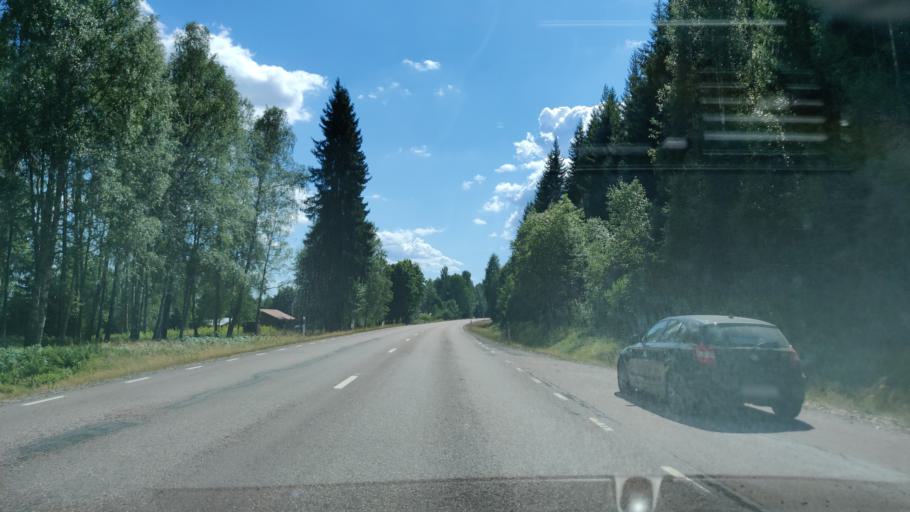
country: SE
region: Vaermland
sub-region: Hagfors Kommun
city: Ekshaerad
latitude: 60.1889
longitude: 13.4976
